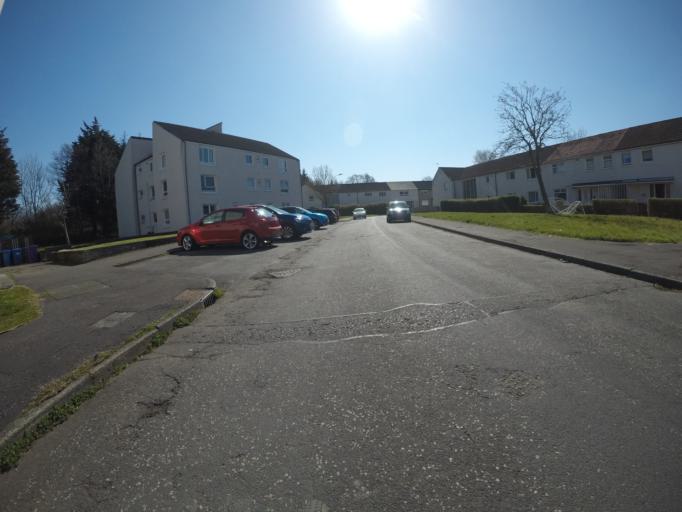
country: GB
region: Scotland
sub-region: North Ayrshire
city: Irvine
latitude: 55.6283
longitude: -4.6567
